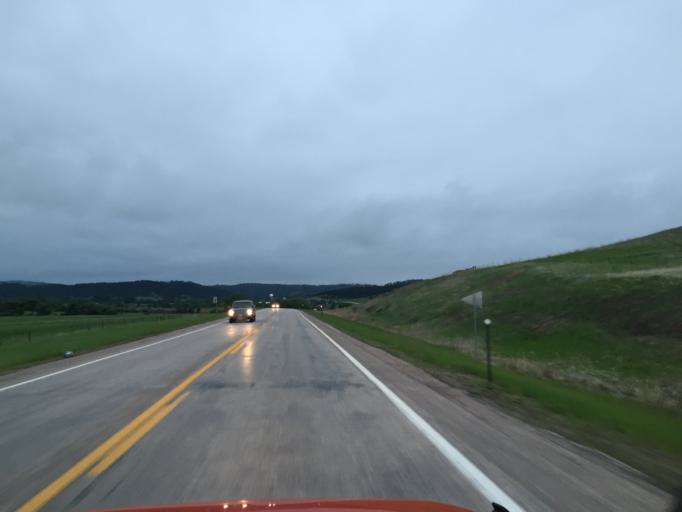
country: US
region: South Dakota
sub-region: Pennington County
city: Colonial Pine Hills
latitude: 43.8365
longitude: -103.2021
